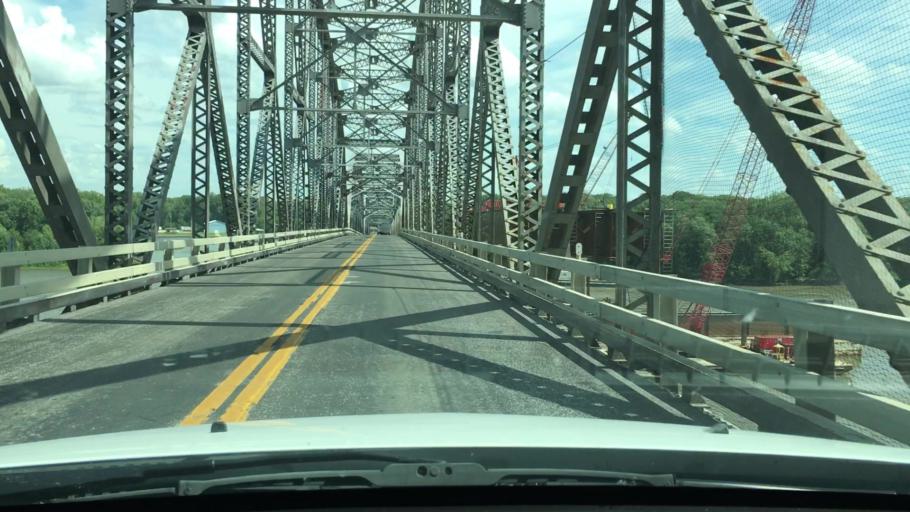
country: US
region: Missouri
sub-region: Pike County
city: Louisiana
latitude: 39.4559
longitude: -91.0494
